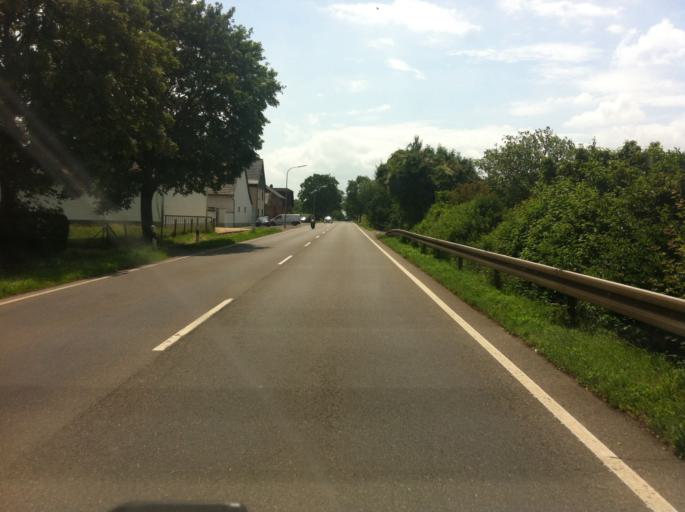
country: DE
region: North Rhine-Westphalia
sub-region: Regierungsbezirk Koln
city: Weilerswist
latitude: 50.7338
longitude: 6.8307
